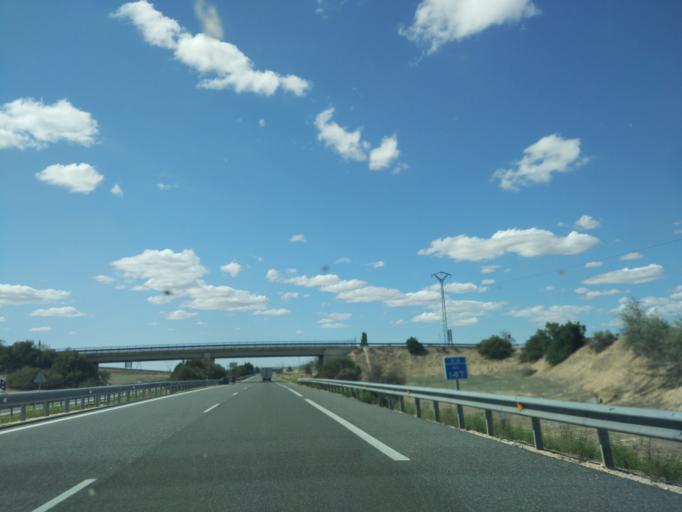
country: ES
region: Castille and Leon
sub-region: Provincia de Valladolid
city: San Vicente del Palacio
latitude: 41.2209
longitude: -4.8429
